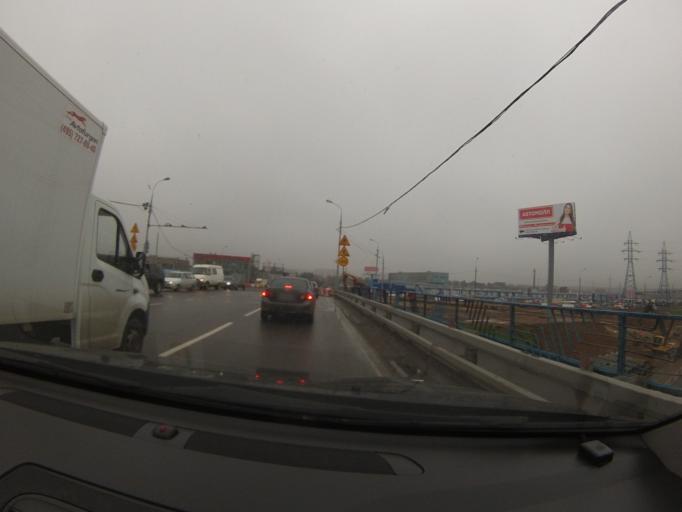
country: RU
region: Moskovskaya
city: Nemchinovka
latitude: 55.7235
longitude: 37.3806
